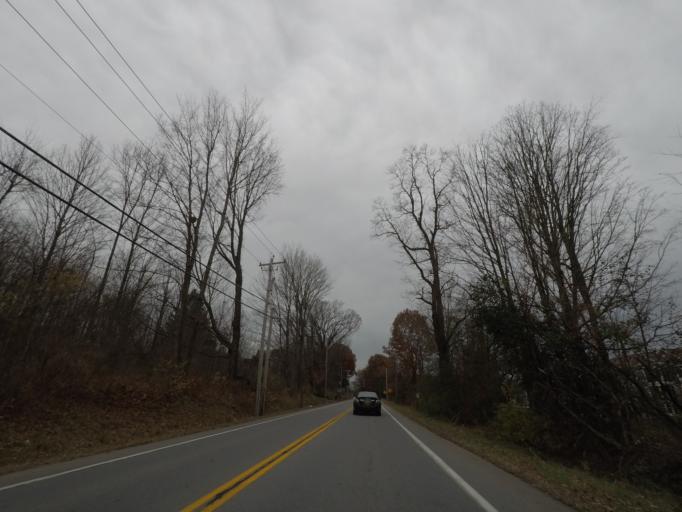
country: US
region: New York
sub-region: Schenectady County
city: Niskayuna
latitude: 42.8350
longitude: -73.8220
